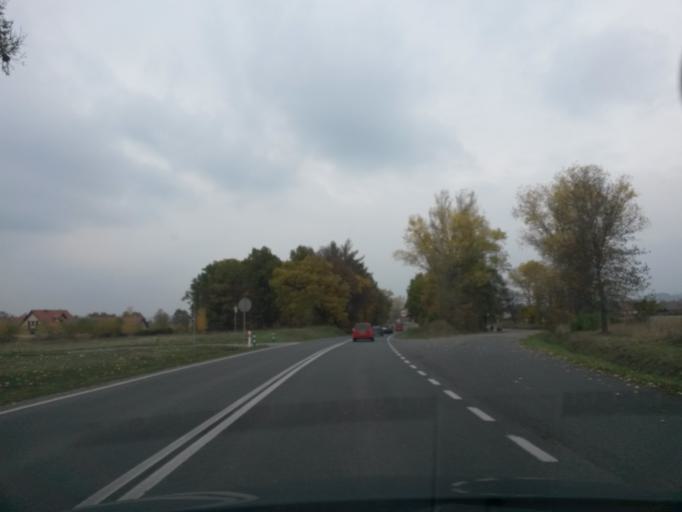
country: PL
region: Lower Silesian Voivodeship
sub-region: Powiat klodzki
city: Klodzko
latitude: 50.4100
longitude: 16.6590
